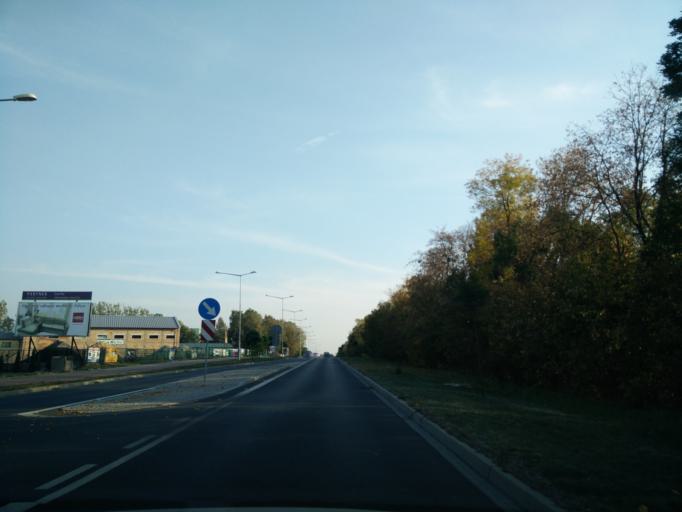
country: PL
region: Greater Poland Voivodeship
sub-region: Powiat sredzki
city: Sroda Wielkopolska
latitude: 52.2195
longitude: 17.2892
